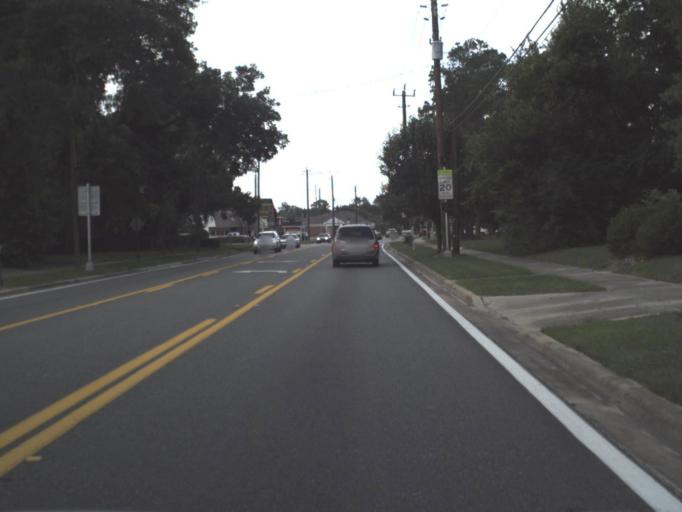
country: US
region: Florida
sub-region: Baker County
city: Macclenny
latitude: 30.2775
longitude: -82.1228
